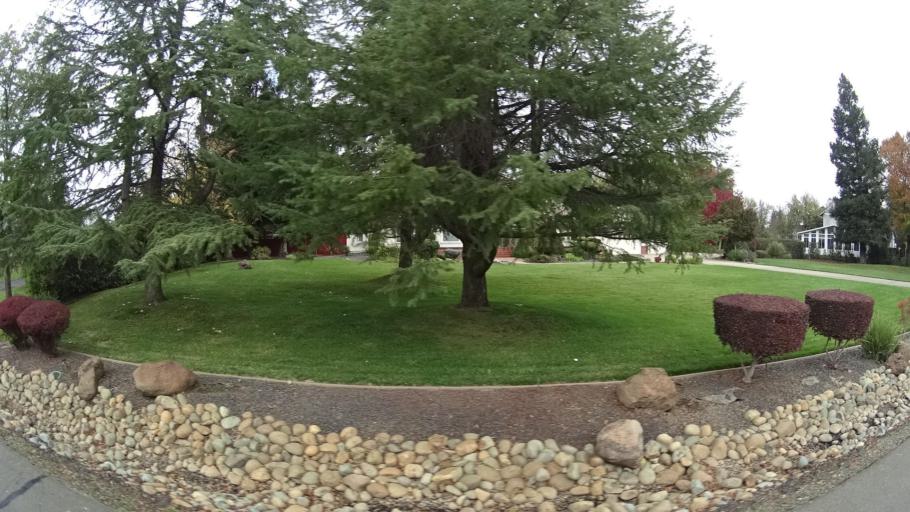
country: US
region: California
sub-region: Sacramento County
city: Vineyard
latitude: 38.4495
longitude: -121.3065
